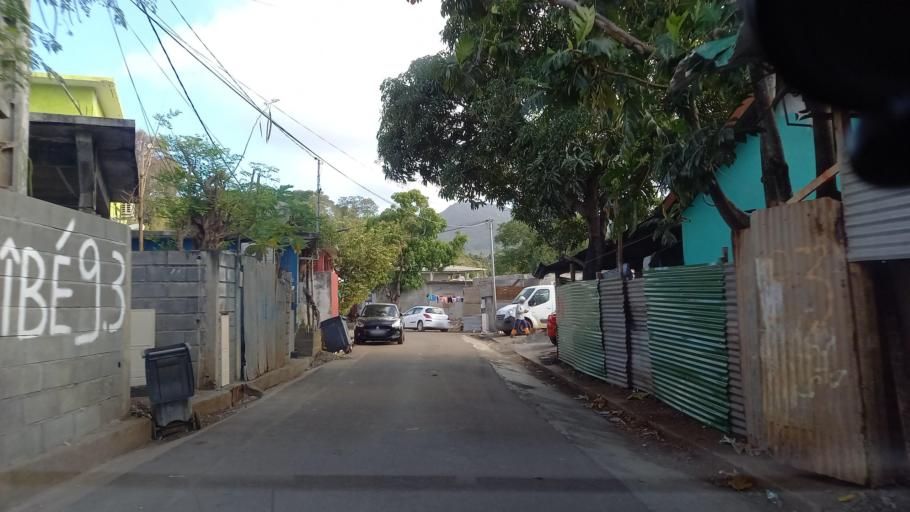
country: YT
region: Bandrele
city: Bandrele
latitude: -12.9085
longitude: 45.1940
